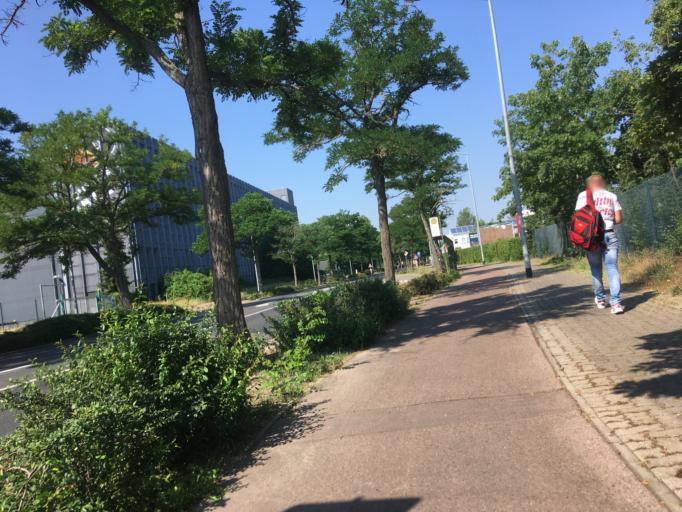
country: DE
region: Saxony-Anhalt
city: Dessau
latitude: 51.8180
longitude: 12.2368
